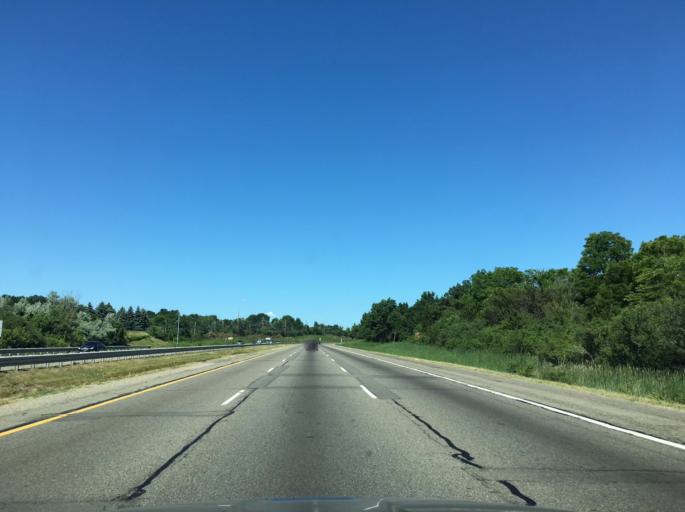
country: US
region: Michigan
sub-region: Oakland County
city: Troy
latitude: 42.6049
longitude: -83.1934
